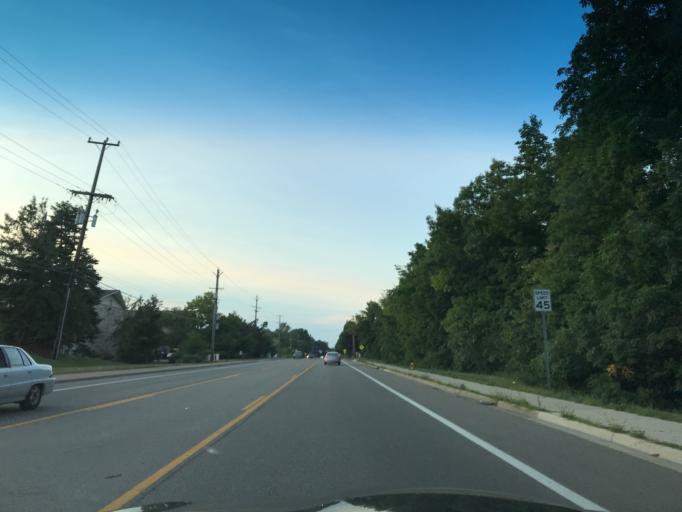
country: US
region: Michigan
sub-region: Washtenaw County
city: Ypsilanti
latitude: 42.2544
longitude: -83.6611
